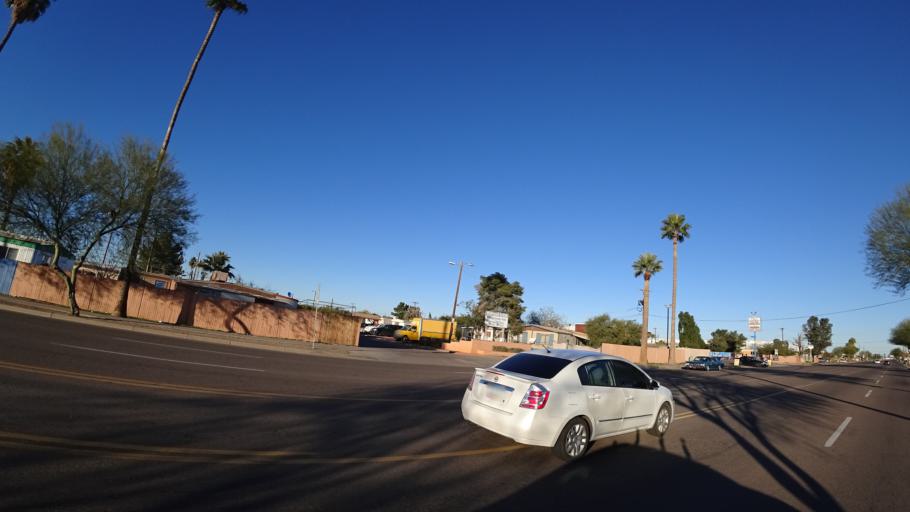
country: US
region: Arizona
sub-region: Maricopa County
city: Tolleson
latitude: 33.4515
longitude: -112.2003
